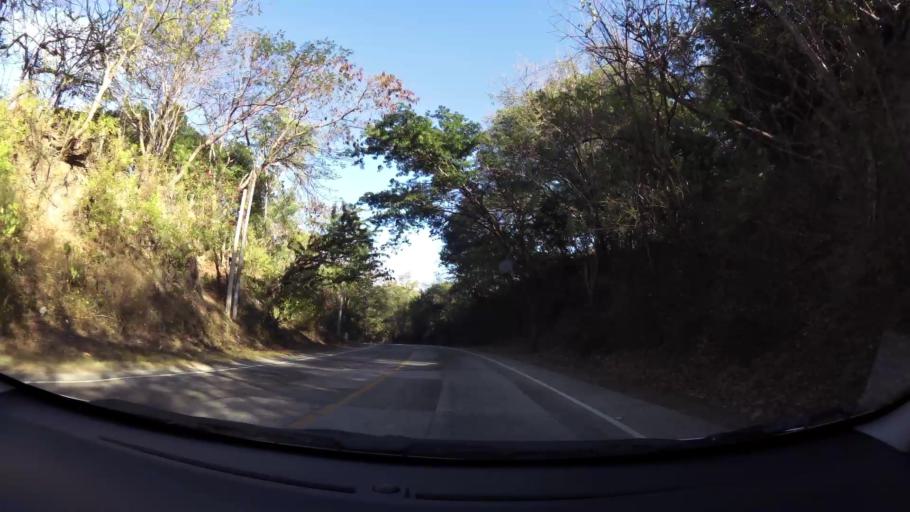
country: SV
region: Santa Ana
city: Texistepeque
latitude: 14.1555
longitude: -89.5096
